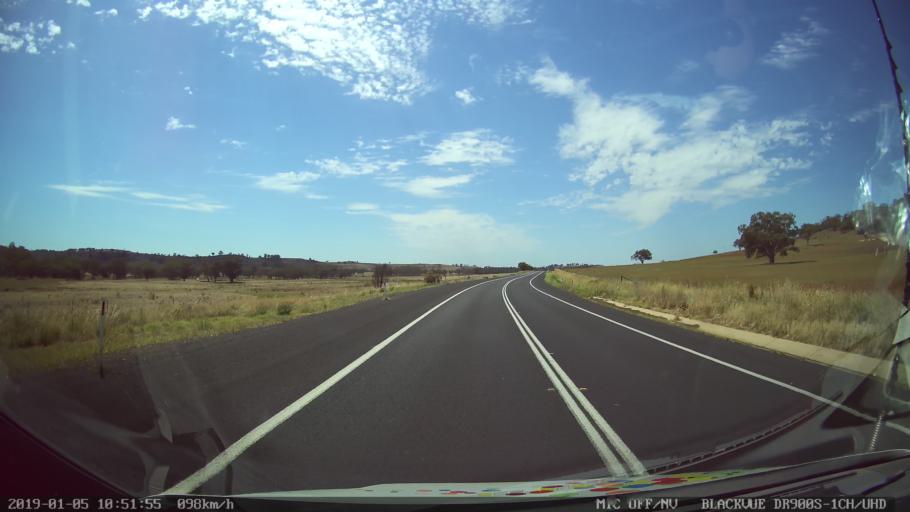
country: AU
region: New South Wales
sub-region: Warrumbungle Shire
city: Coonabarabran
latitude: -31.4258
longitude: 149.0977
